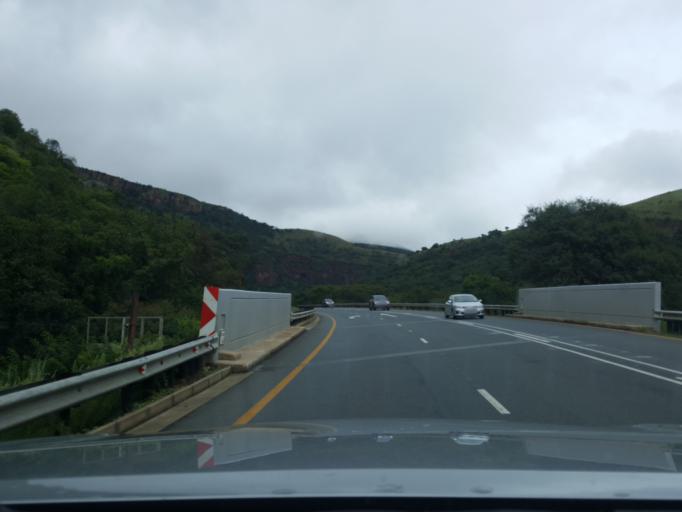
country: ZA
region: Mpumalanga
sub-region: Nkangala District Municipality
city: Belfast
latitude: -25.6450
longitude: 30.3705
